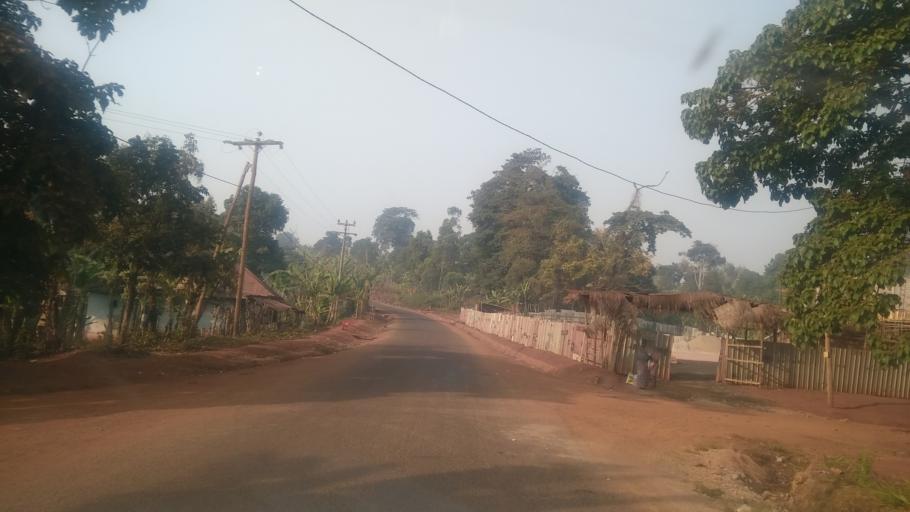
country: CM
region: West
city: Bandjoun
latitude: 5.3364
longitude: 10.4034
